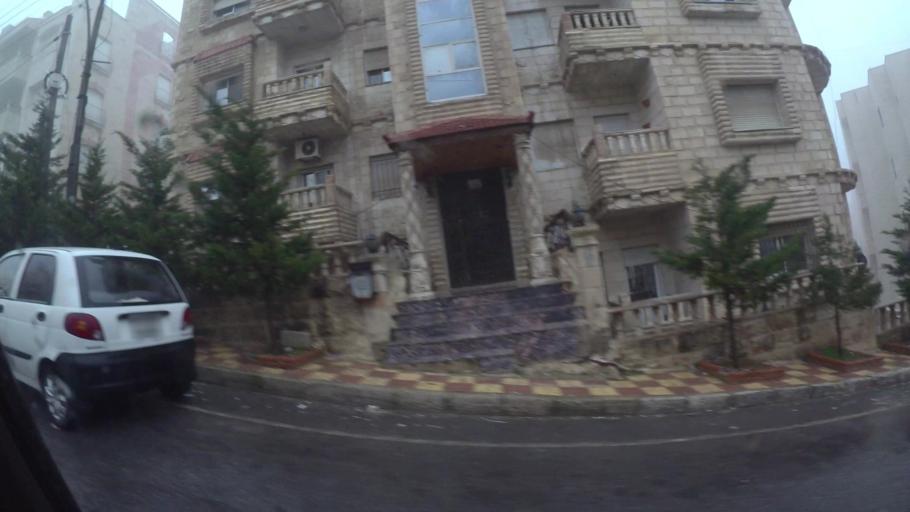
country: JO
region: Amman
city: Al Jubayhah
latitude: 32.0064
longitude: 35.8811
